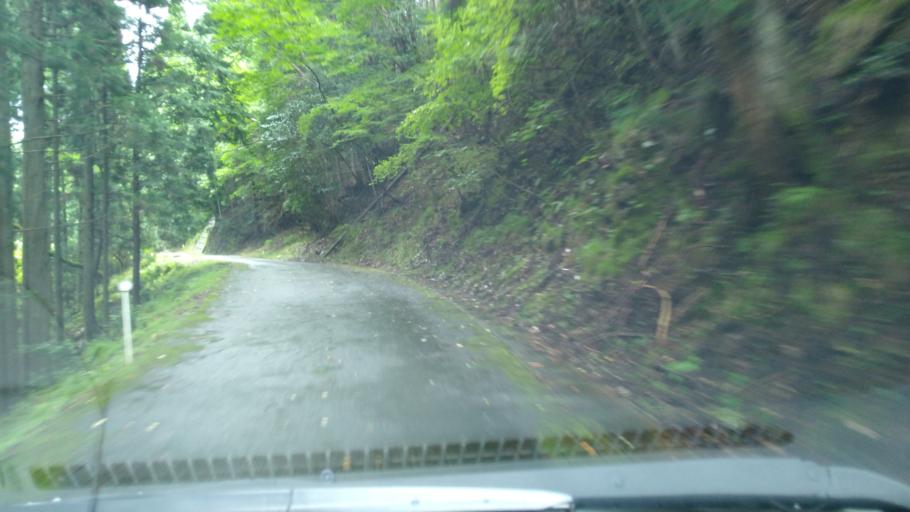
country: JP
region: Kyoto
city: Ayabe
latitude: 35.2315
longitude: 135.2682
